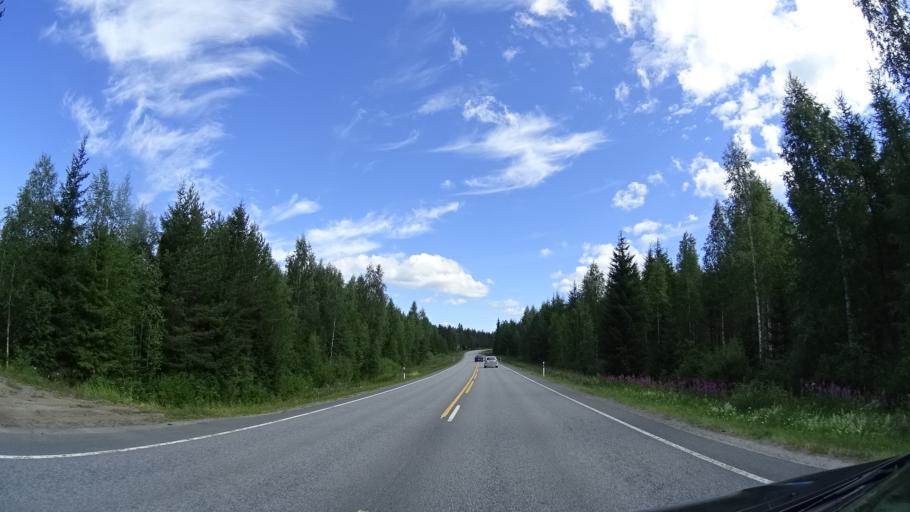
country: FI
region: Pirkanmaa
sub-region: Luoteis-Pirkanmaa
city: Kihnioe
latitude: 62.1393
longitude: 23.1452
